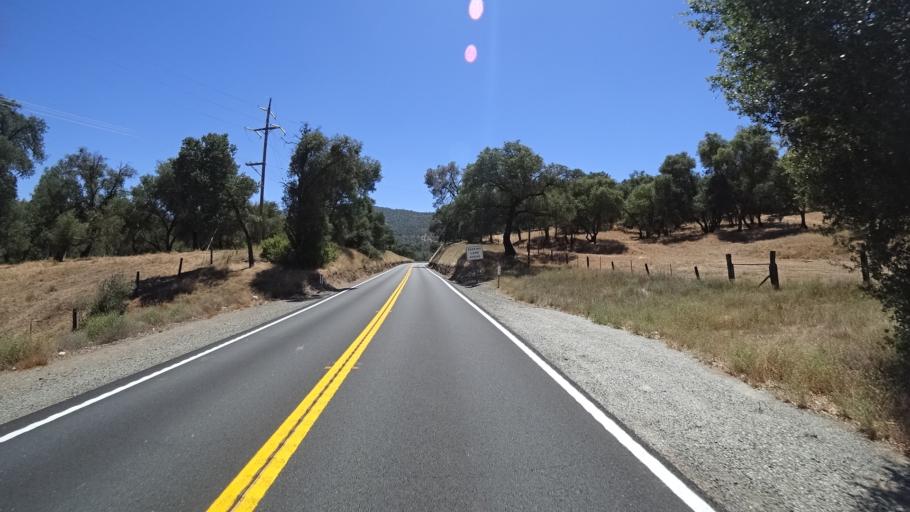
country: US
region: California
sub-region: Calaveras County
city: San Andreas
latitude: 38.2043
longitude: -120.7140
